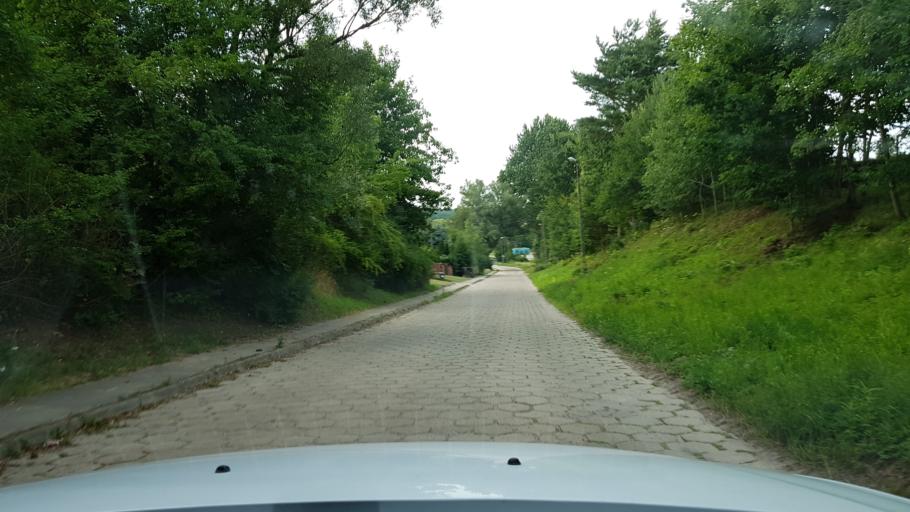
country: PL
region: West Pomeranian Voivodeship
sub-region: Powiat swidwinski
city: Polczyn-Zdroj
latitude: 53.7754
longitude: 16.0939
